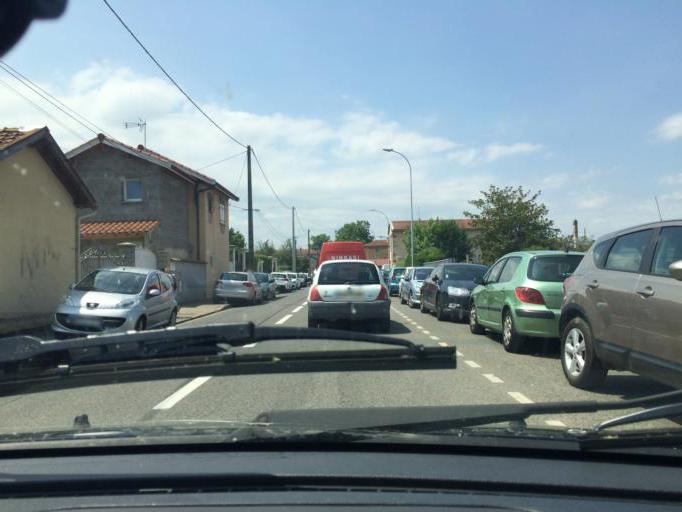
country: FR
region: Rhone-Alpes
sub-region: Departement de l'Ain
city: Jassans-Riottier
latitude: 45.9734
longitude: 4.7498
